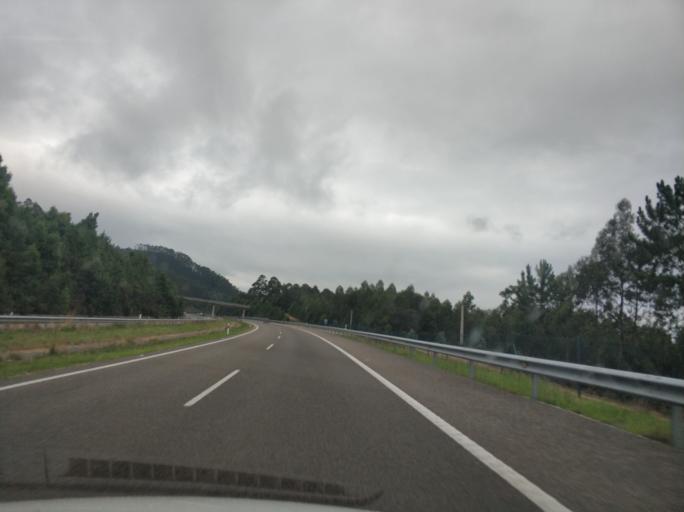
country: ES
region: Galicia
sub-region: Provincia de Lugo
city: Ribadeo
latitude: 43.5351
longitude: -7.1142
